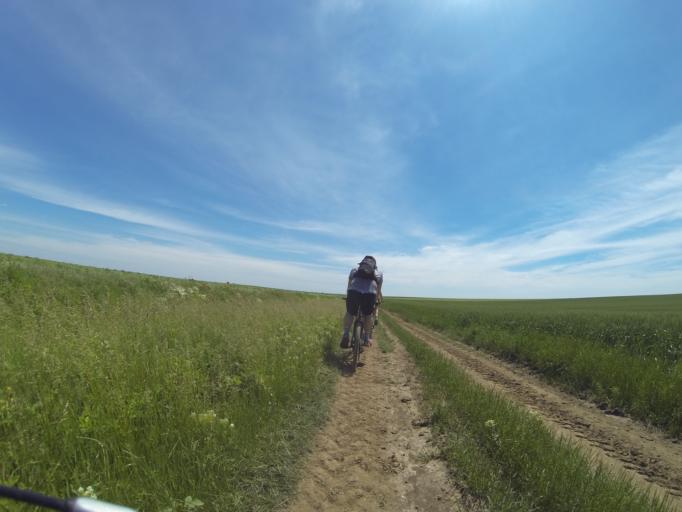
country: RO
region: Dolj
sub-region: Comuna Leu
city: Leu
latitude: 44.1883
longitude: 24.0518
